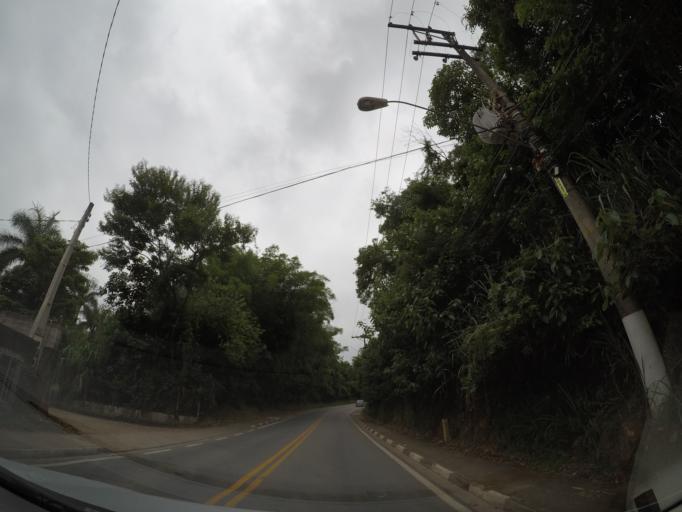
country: BR
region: Sao Paulo
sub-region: Louveira
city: Louveira
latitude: -23.0755
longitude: -46.9595
